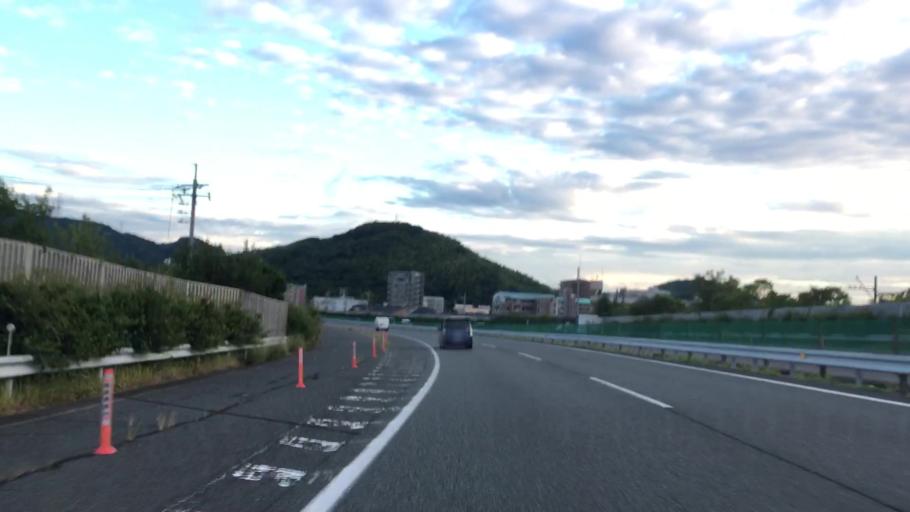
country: JP
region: Yamaguchi
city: Shimonoseki
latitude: 34.0136
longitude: 130.9558
